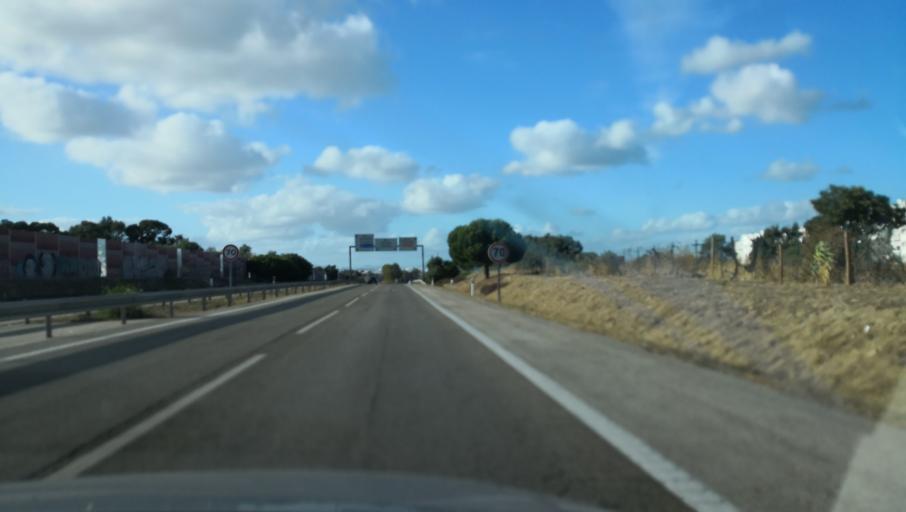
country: PT
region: Setubal
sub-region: Barreiro
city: Barreiro
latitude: 38.6532
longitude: -9.0534
